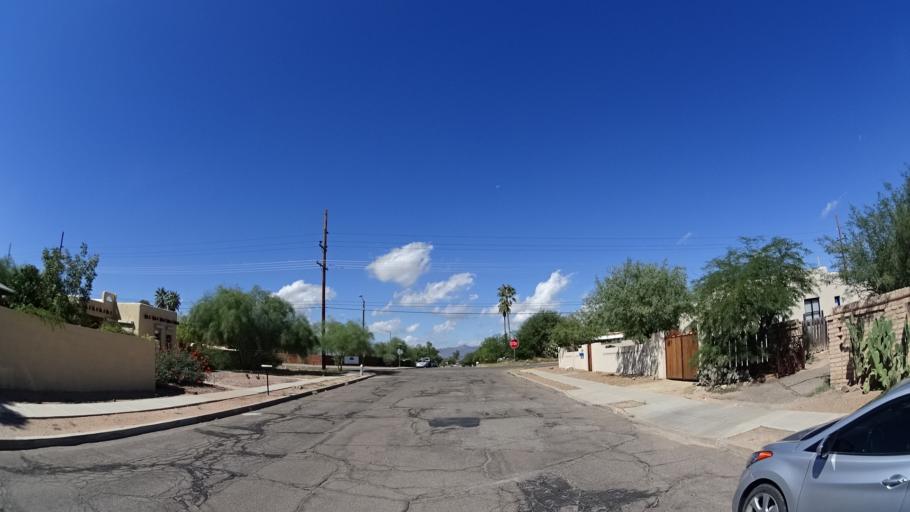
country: US
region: Arizona
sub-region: Pima County
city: Tucson
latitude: 32.2468
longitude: -110.9563
